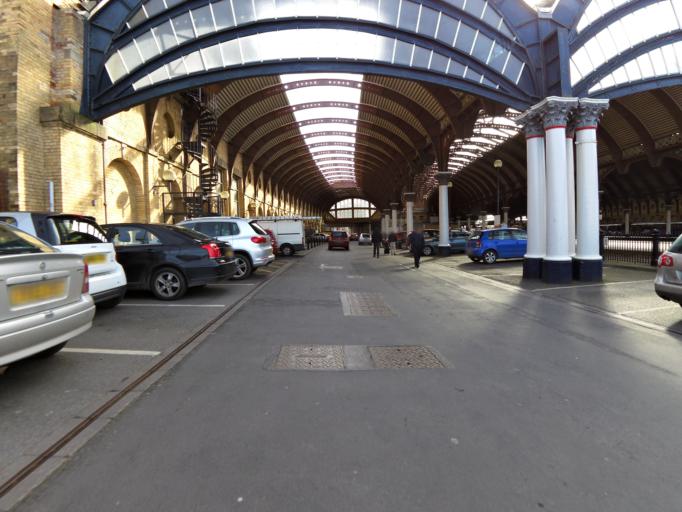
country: GB
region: England
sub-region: City of York
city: York
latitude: 53.9593
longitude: -1.0927
